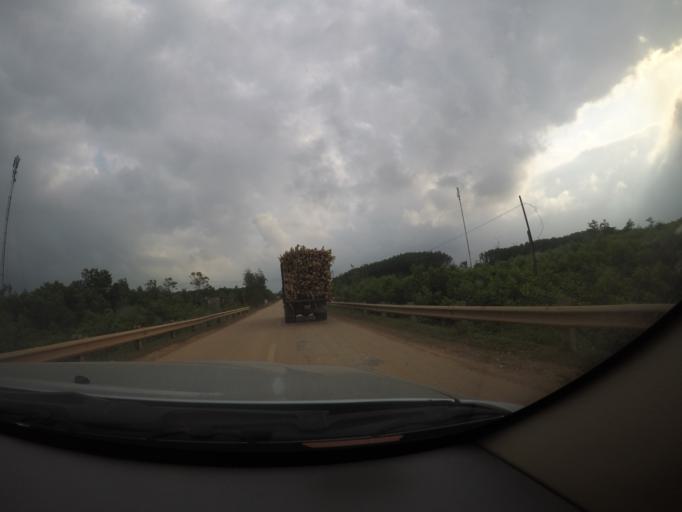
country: VN
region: Quang Tri
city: Ho Xa
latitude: 17.0785
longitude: 106.8618
